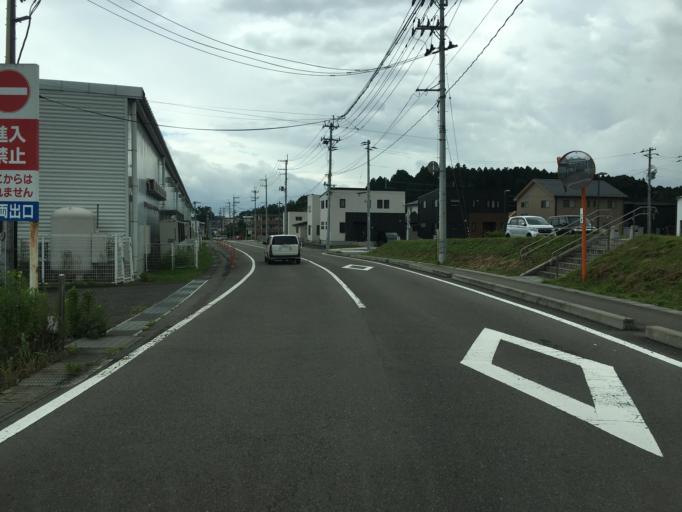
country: JP
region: Fukushima
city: Nihommatsu
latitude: 37.6163
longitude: 140.4605
